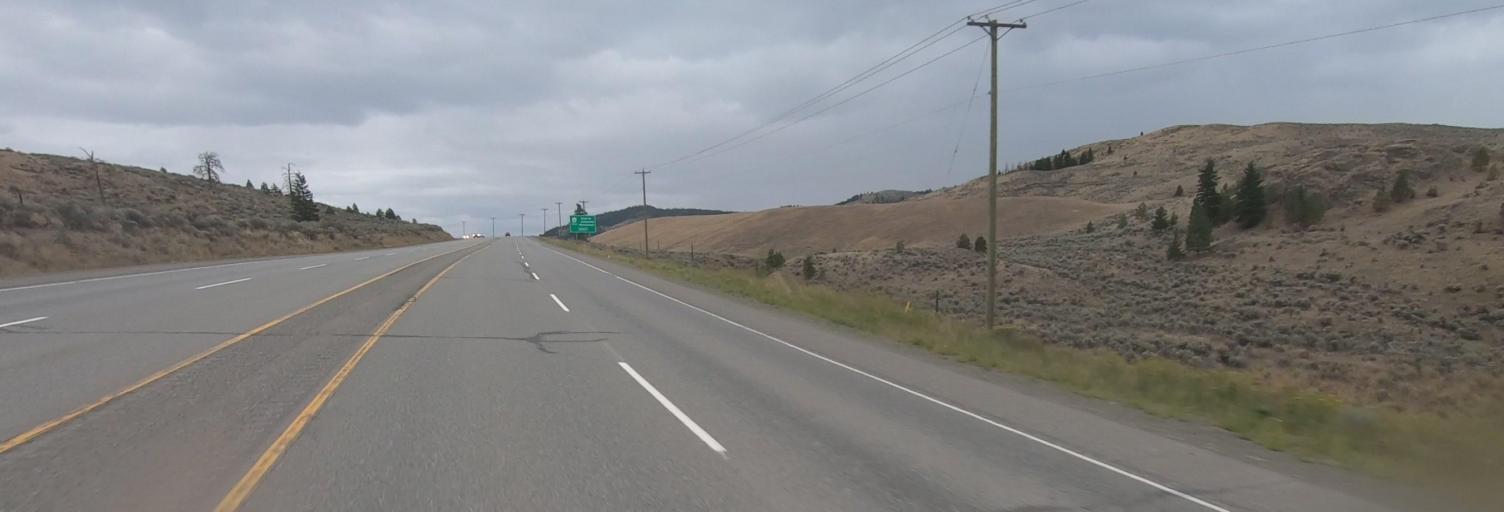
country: CA
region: British Columbia
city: Kamloops
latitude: 50.6700
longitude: -120.4813
